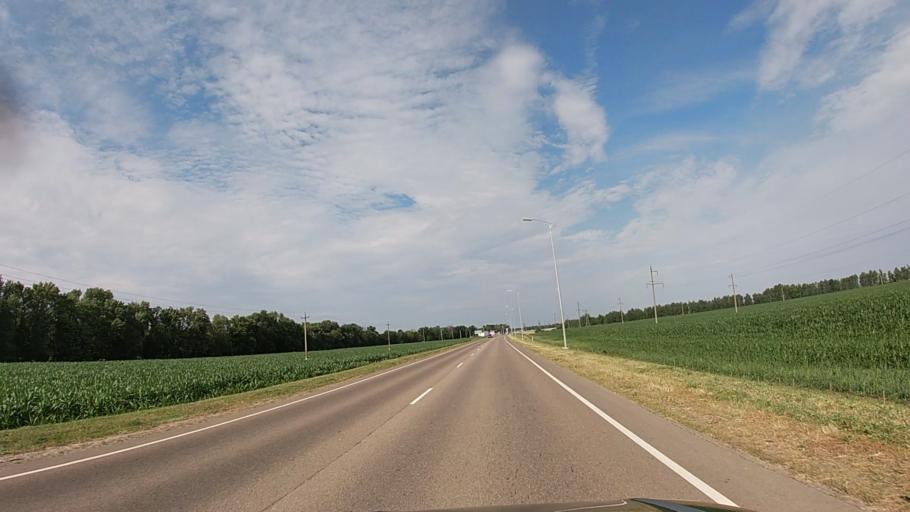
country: RU
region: Belgorod
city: Proletarskiy
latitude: 50.7984
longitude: 35.7235
